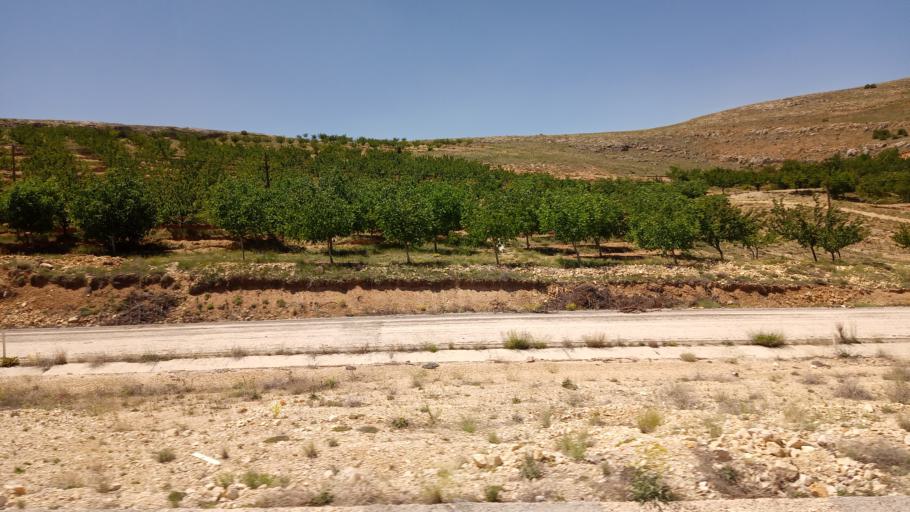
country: TR
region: Malatya
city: Darende
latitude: 38.6345
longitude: 37.4509
